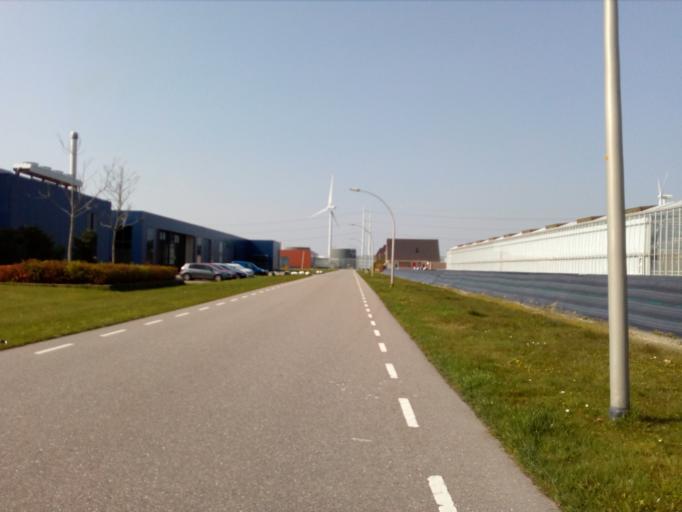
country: NL
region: South Holland
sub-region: Gemeente Lansingerland
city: Bleiswijk
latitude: 52.0327
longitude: 4.5171
